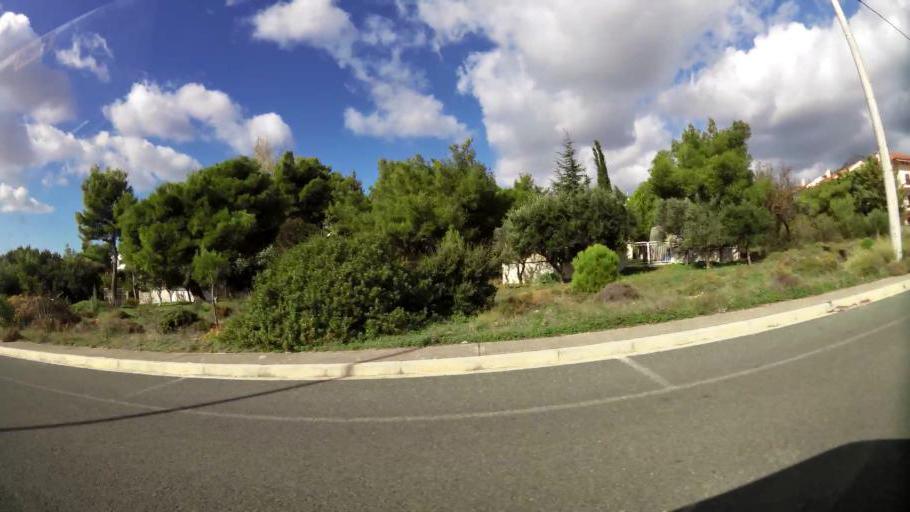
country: GR
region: Attica
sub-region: Nomarchia Anatolikis Attikis
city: Thrakomakedones
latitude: 38.1257
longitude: 23.7672
